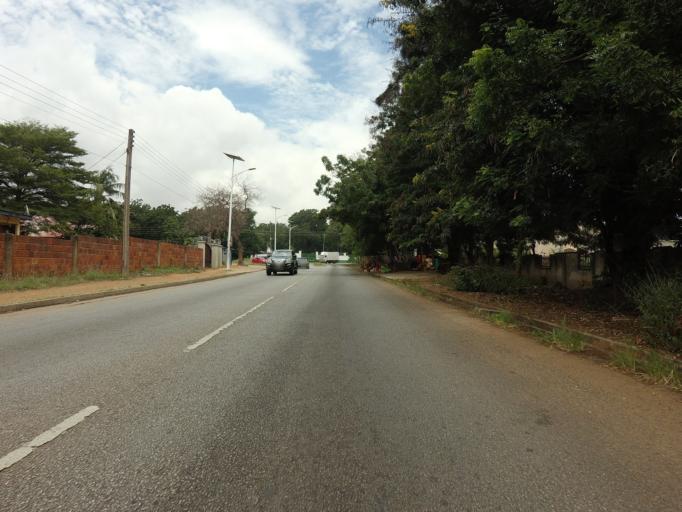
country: GH
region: Greater Accra
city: Accra
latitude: 5.5797
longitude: -0.1756
